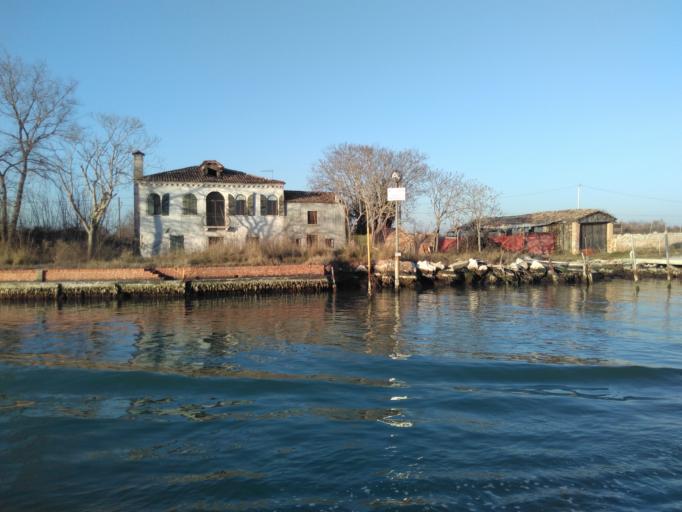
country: IT
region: Veneto
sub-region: Provincia di Venezia
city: Burano
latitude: 45.4876
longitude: 12.4073
